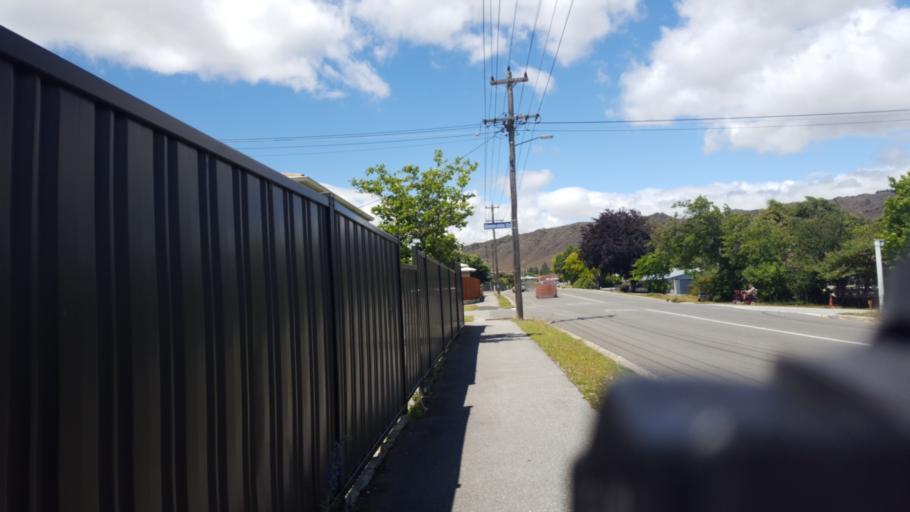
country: NZ
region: Otago
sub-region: Queenstown-Lakes District
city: Wanaka
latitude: -45.2473
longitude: 169.3904
